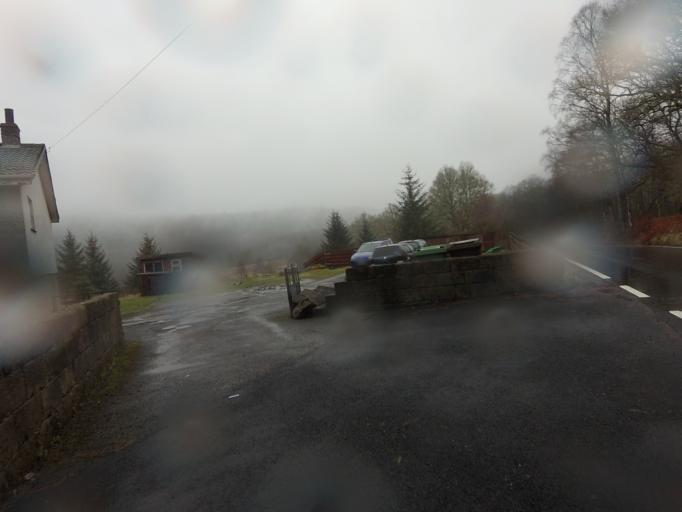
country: GB
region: Scotland
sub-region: Stirling
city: Killearn
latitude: 56.1912
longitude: -4.5046
